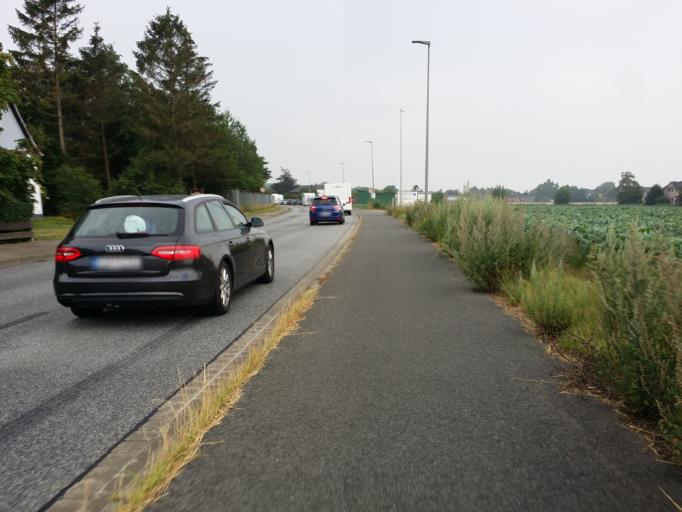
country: DE
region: Schleswig-Holstein
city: Blomesche Wildnis
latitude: 53.8065
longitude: 9.4178
